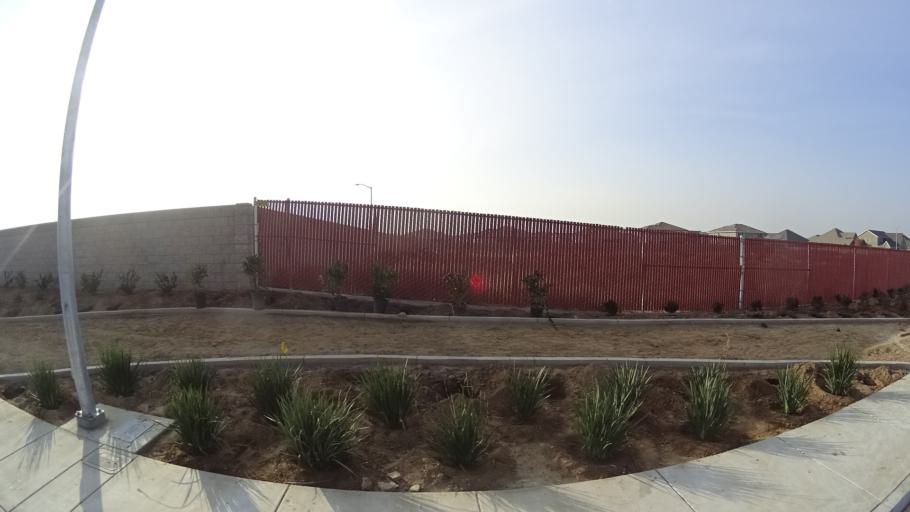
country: US
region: California
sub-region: Kern County
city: Greenacres
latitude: 35.4342
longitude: -119.1044
